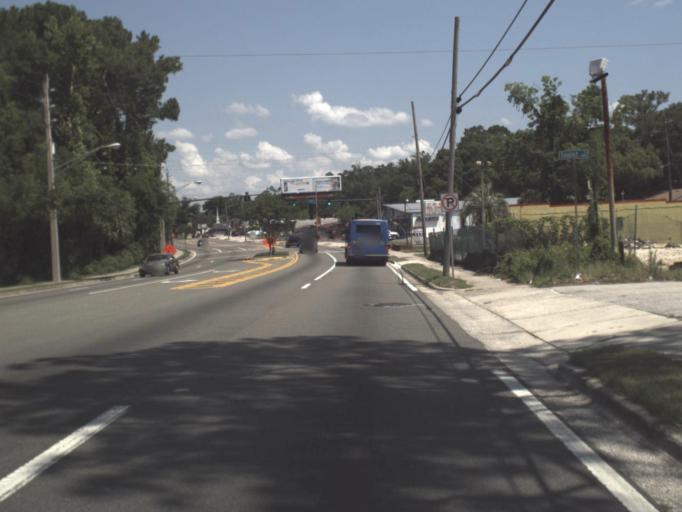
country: US
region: Florida
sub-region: Duval County
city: Jacksonville
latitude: 30.4012
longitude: -81.6839
